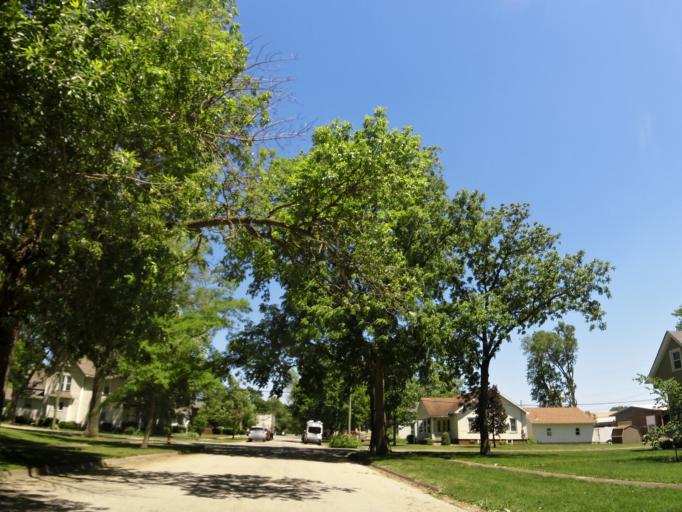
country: US
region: Illinois
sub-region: Livingston County
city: Forrest
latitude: 40.7504
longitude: -88.4127
